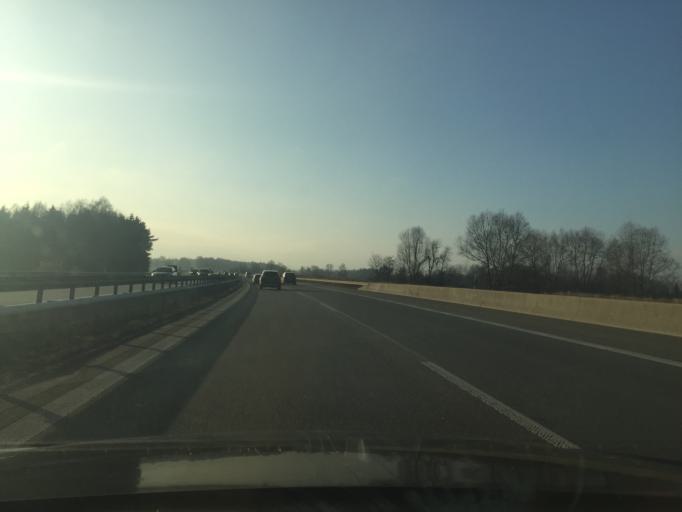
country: DE
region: Bavaria
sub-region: Upper Bavaria
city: Ubersee
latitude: 47.8372
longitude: 12.4509
